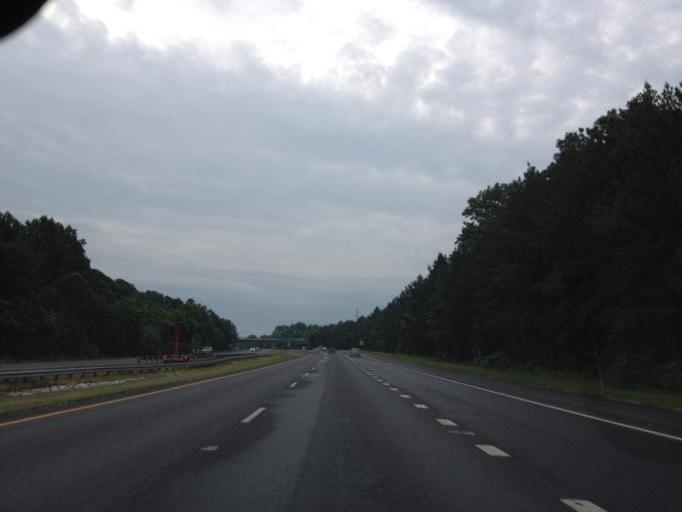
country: US
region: Maryland
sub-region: Anne Arundel County
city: Crownsville
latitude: 39.0511
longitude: -76.6265
